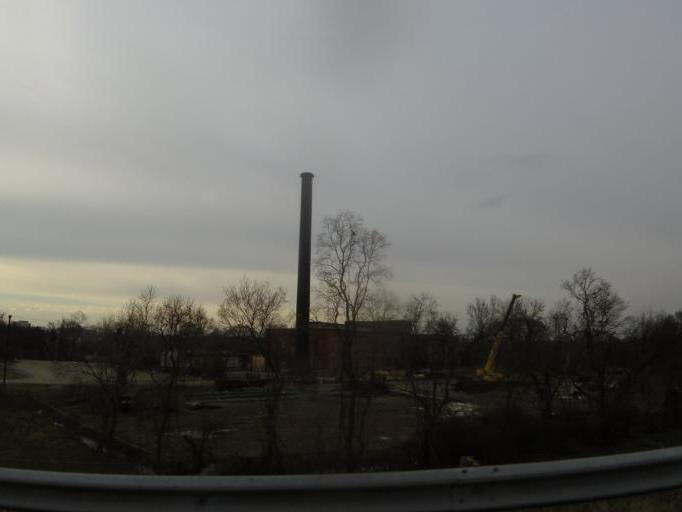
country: US
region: Alabama
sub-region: Montgomery County
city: Montgomery
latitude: 32.3946
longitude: -86.3166
